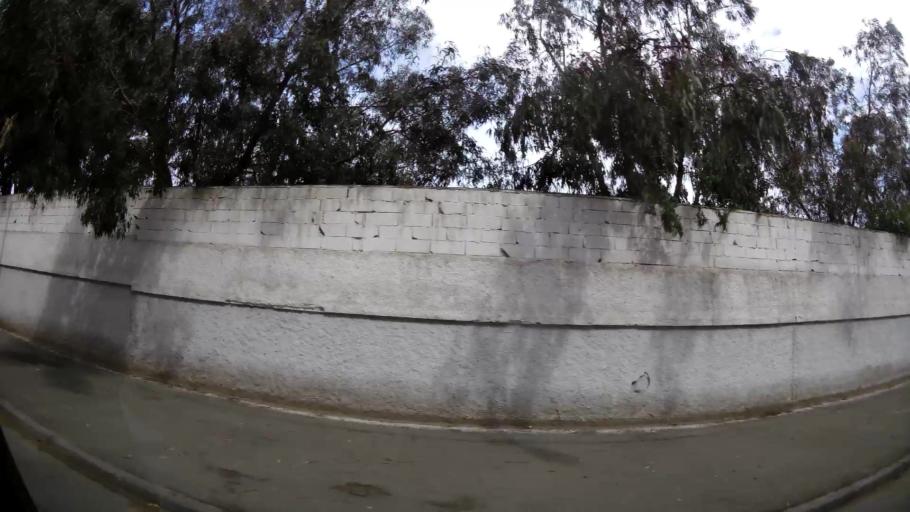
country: MA
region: Grand Casablanca
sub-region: Casablanca
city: Casablanca
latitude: 33.5773
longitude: -7.5839
